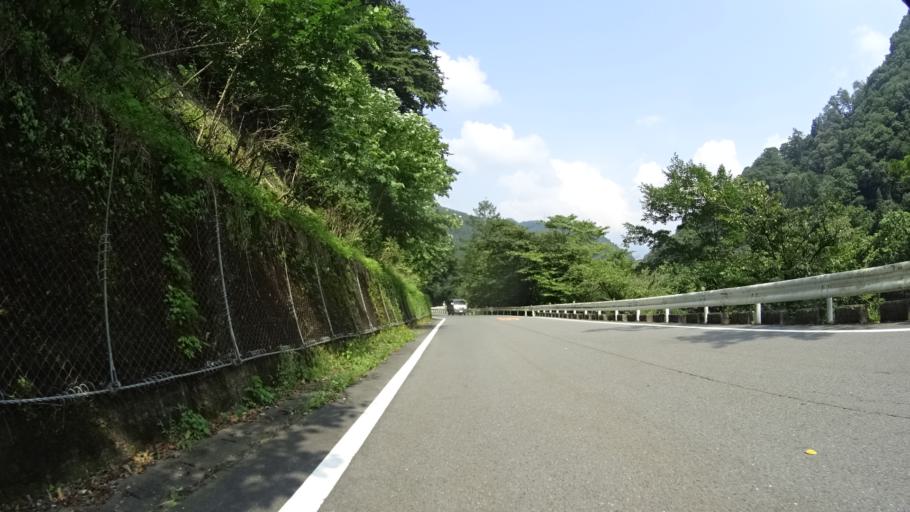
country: JP
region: Gunma
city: Tomioka
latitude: 36.0610
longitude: 138.8364
